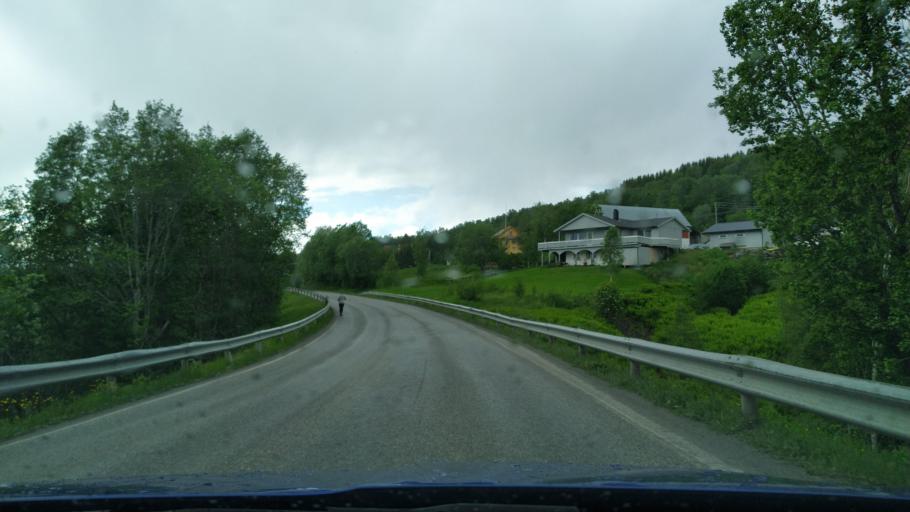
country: NO
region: Troms
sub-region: Sorreisa
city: Sorreisa
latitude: 69.1584
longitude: 18.1586
